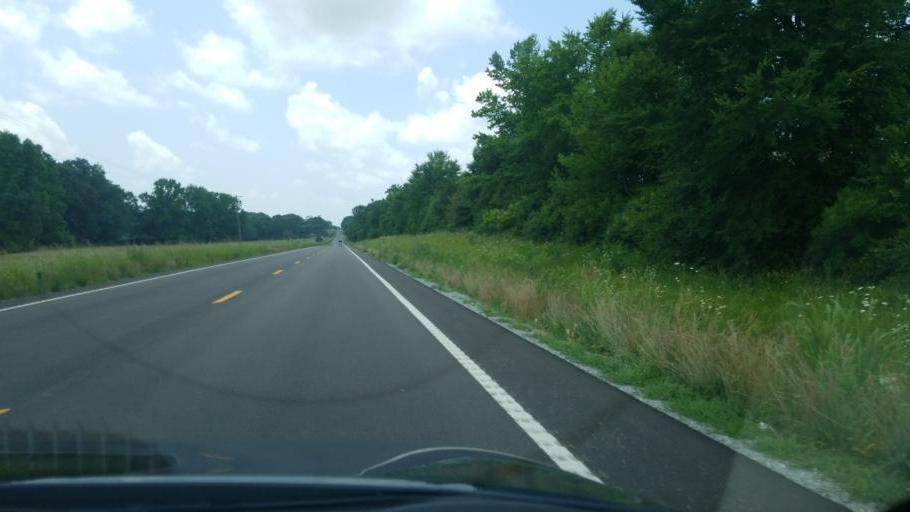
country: US
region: Tennessee
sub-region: Carroll County
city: Huntingdon
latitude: 36.0272
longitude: -88.3615
